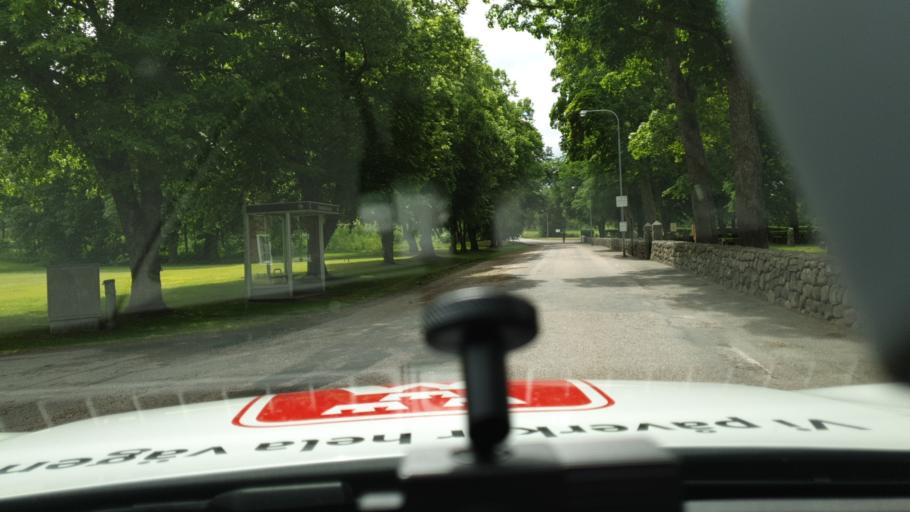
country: SE
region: Vaestra Goetaland
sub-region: Karlsborgs Kommun
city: Molltorp
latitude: 58.6590
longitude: 14.3999
